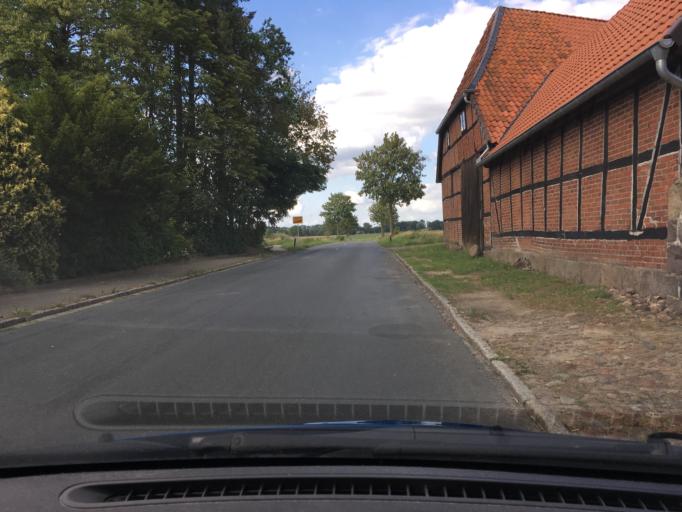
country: DE
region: Lower Saxony
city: Altenmedingen
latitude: 53.1325
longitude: 10.6066
